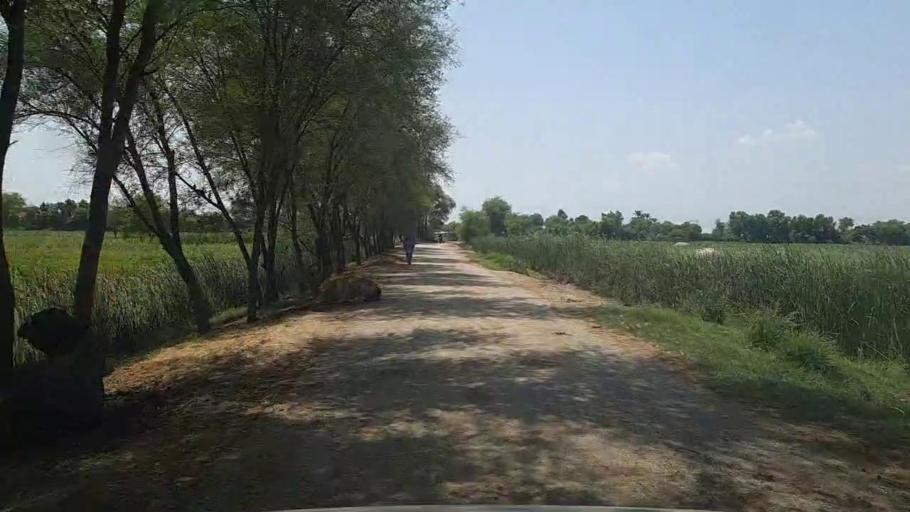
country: PK
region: Sindh
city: Ubauro
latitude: 28.1791
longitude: 69.7079
